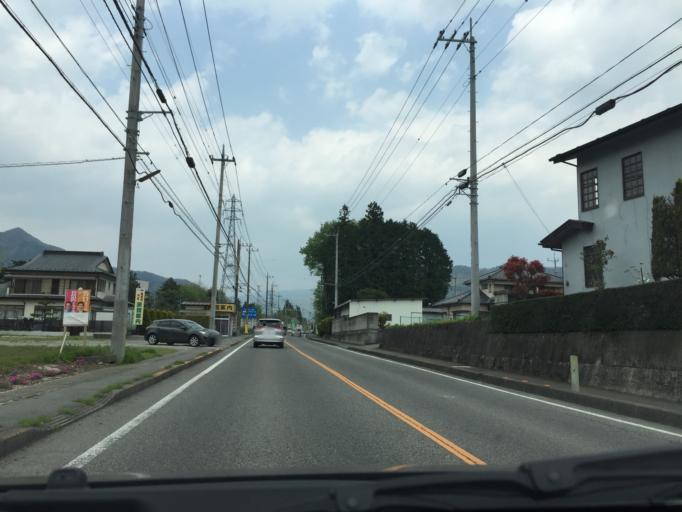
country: JP
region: Tochigi
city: Imaichi
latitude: 36.8047
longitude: 139.7076
